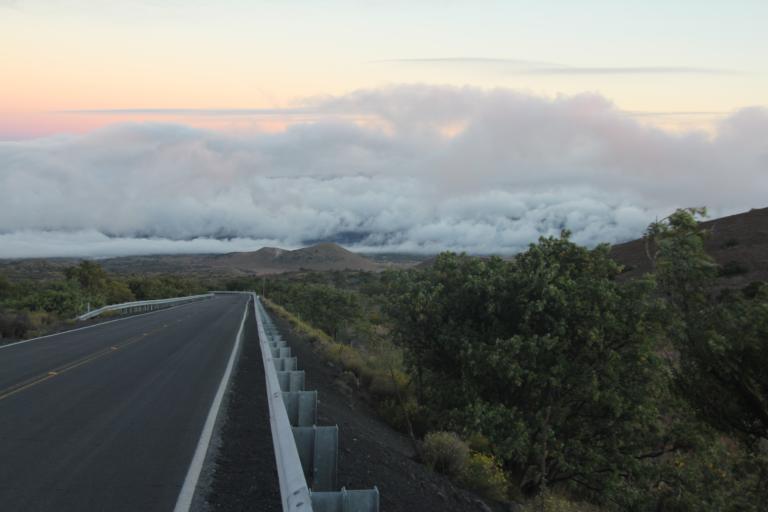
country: US
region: Hawaii
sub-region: Hawaii County
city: Honoka'a
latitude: 19.7477
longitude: -155.4542
